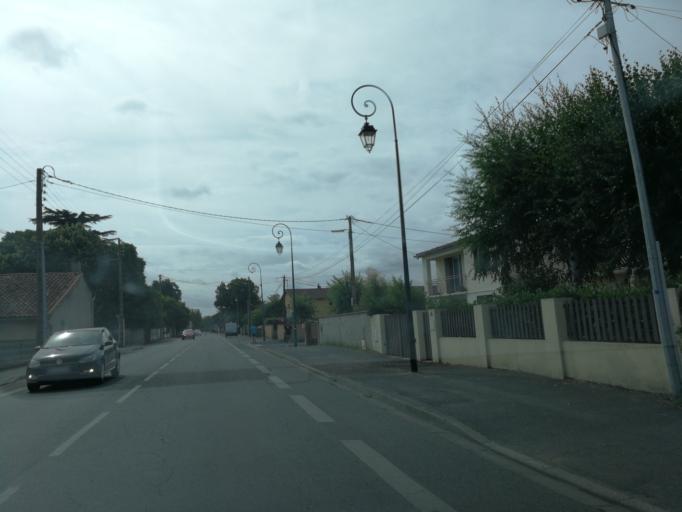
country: FR
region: Midi-Pyrenees
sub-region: Departement de la Haute-Garonne
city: Aucamville
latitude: 43.6722
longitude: 1.4270
